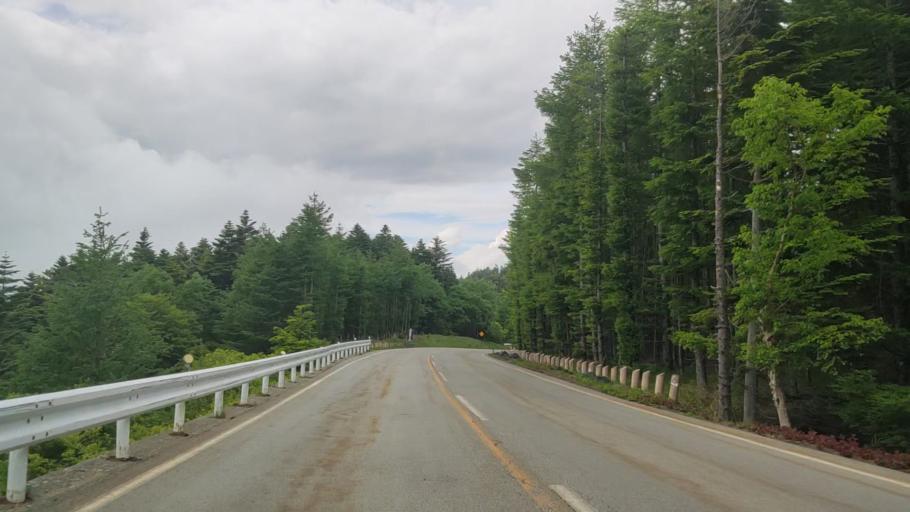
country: JP
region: Yamanashi
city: Fujikawaguchiko
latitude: 35.3871
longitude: 138.6904
